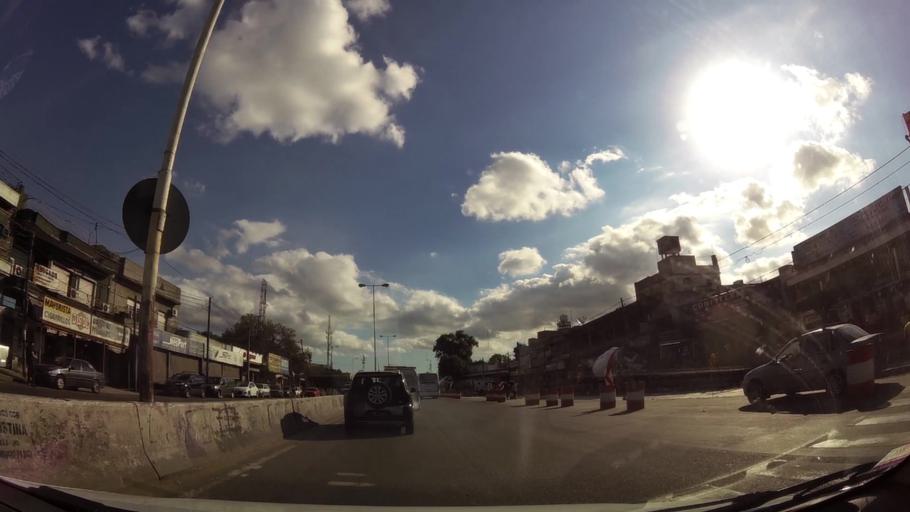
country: AR
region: Buenos Aires
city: San Justo
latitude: -34.7041
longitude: -58.5828
